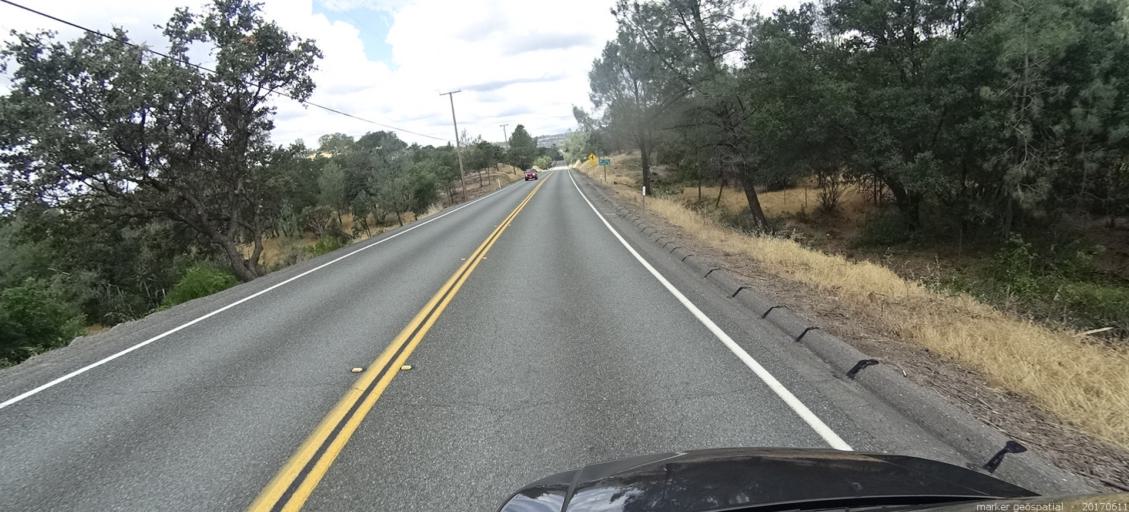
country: US
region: California
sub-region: Butte County
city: Paradise
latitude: 39.6537
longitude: -121.5635
